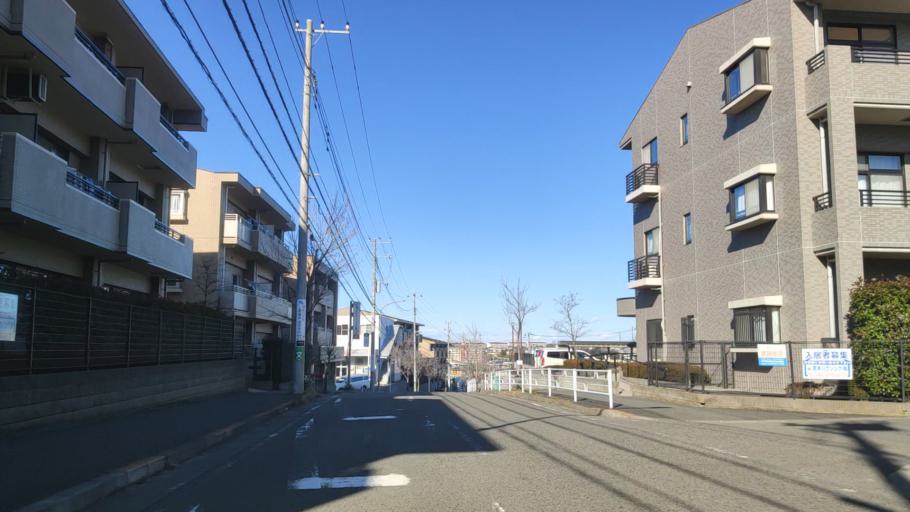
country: JP
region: Kanagawa
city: Minami-rinkan
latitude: 35.5087
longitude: 139.5347
